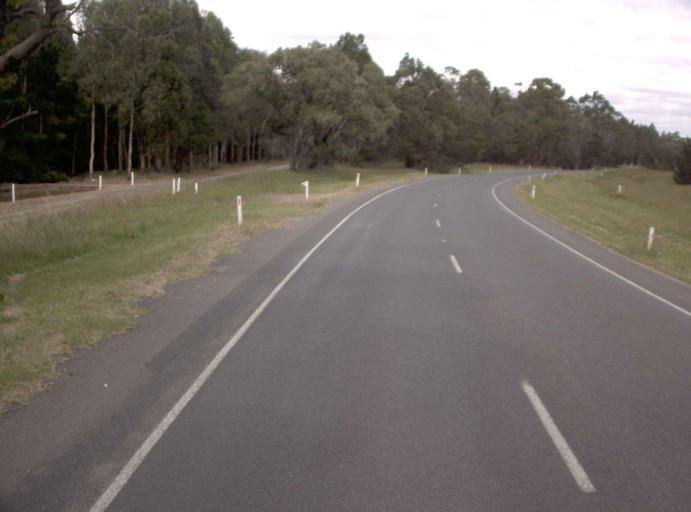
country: AU
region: Victoria
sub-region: Latrobe
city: Traralgon
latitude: -38.1875
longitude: 146.4704
